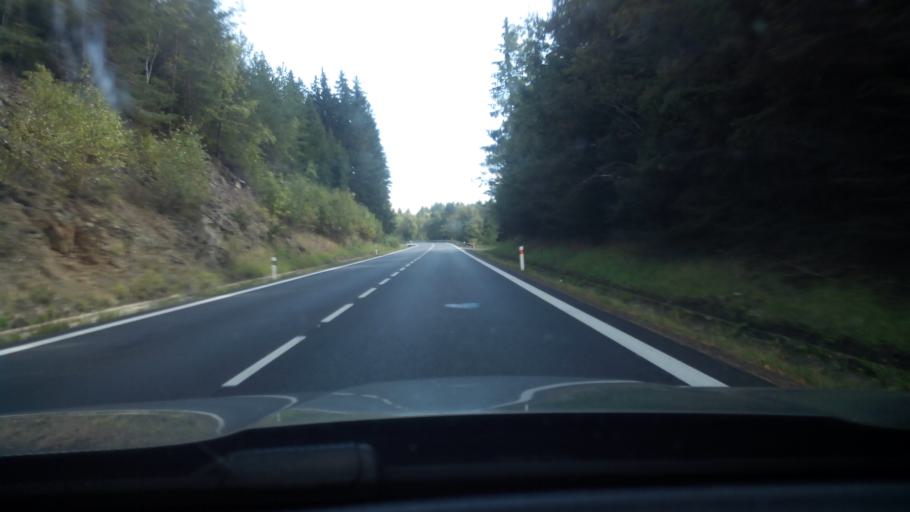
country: CZ
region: Jihocesky
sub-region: Okres Prachatice
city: Zdikov
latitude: 49.0702
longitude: 13.7157
